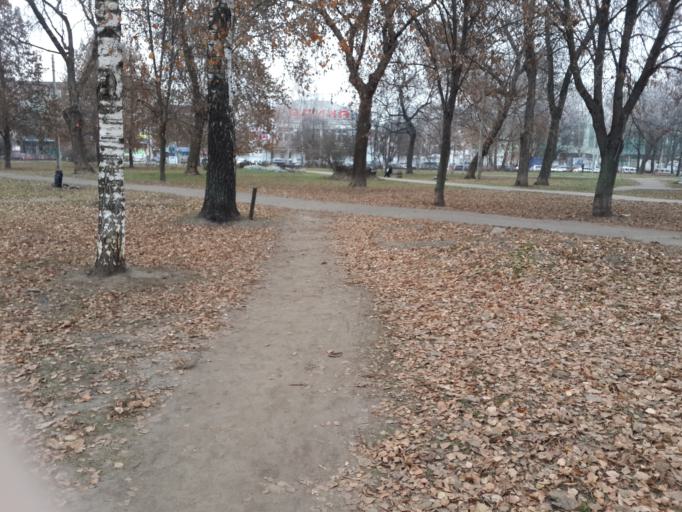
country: RU
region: Jaroslavl
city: Yaroslavl
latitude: 57.6368
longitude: 39.8800
